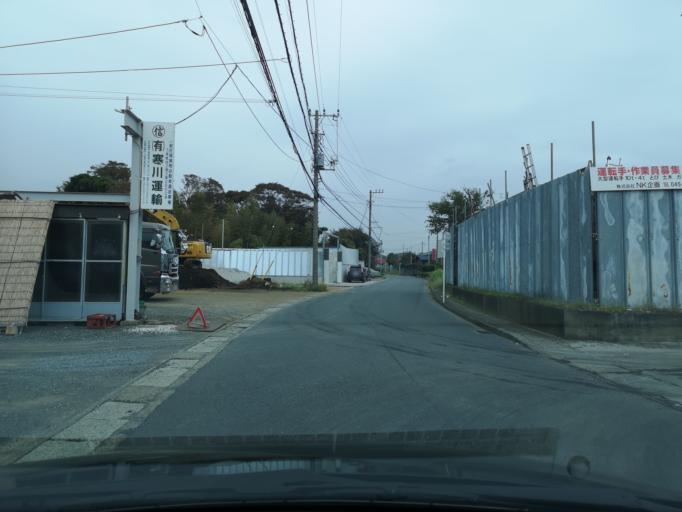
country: JP
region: Kanagawa
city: Chigasaki
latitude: 35.3878
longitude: 139.4005
